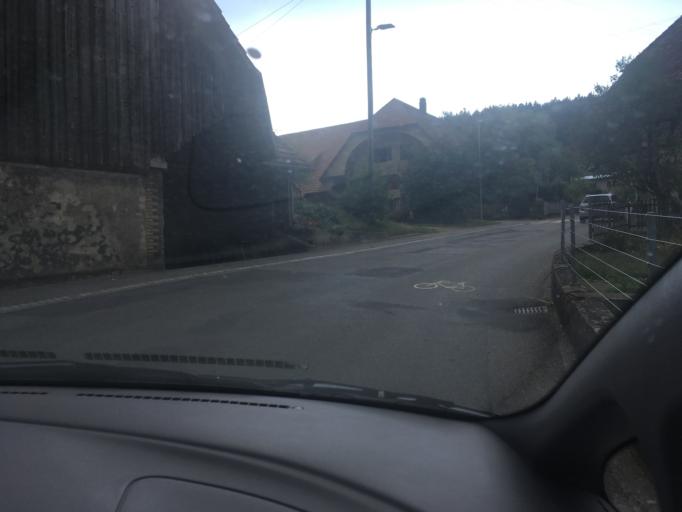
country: CH
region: Bern
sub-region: Seeland District
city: Schupfen
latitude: 47.0090
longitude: 7.3628
